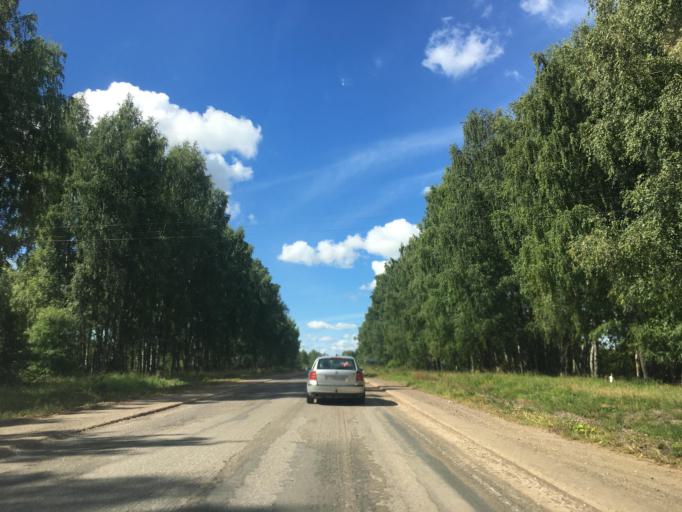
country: RU
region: Pskov
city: Palkino
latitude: 57.5442
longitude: 28.0232
